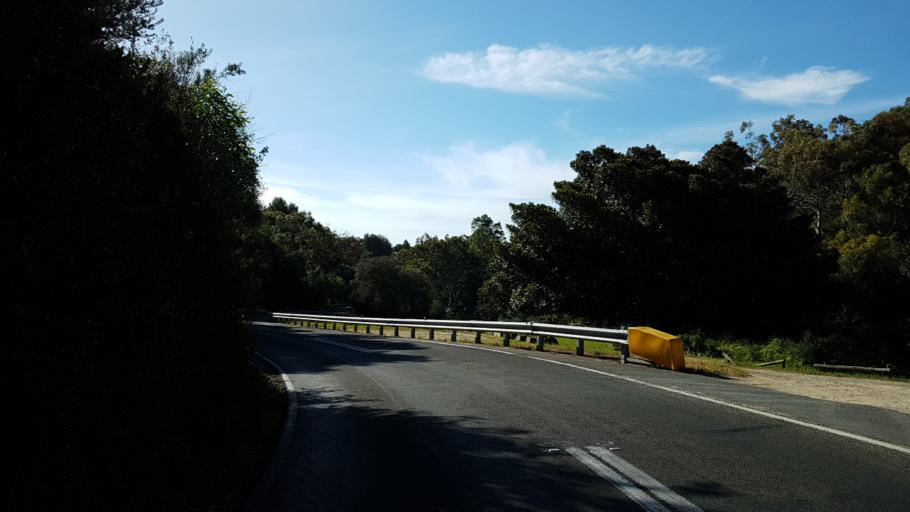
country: AU
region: South Australia
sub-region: Adelaide Hills
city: Adelaide Hills
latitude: -34.9128
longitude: 138.6972
